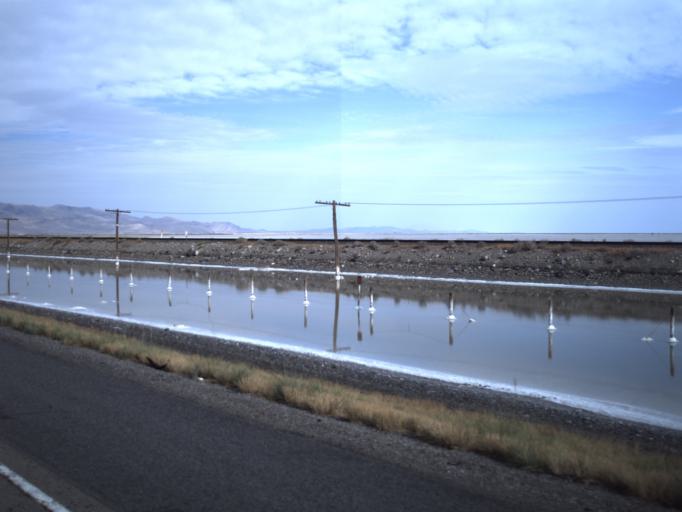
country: US
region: Utah
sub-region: Tooele County
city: Grantsville
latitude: 40.7352
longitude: -112.6048
